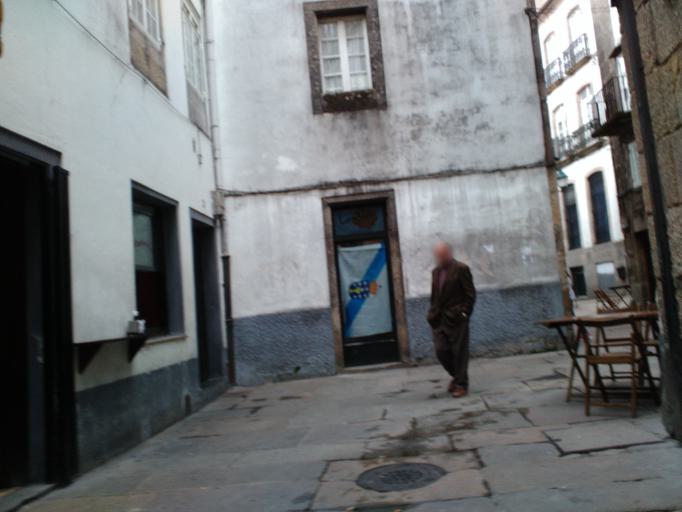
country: ES
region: Galicia
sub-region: Provincia da Coruna
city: Santiago de Compostela
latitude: 42.8786
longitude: -8.5451
